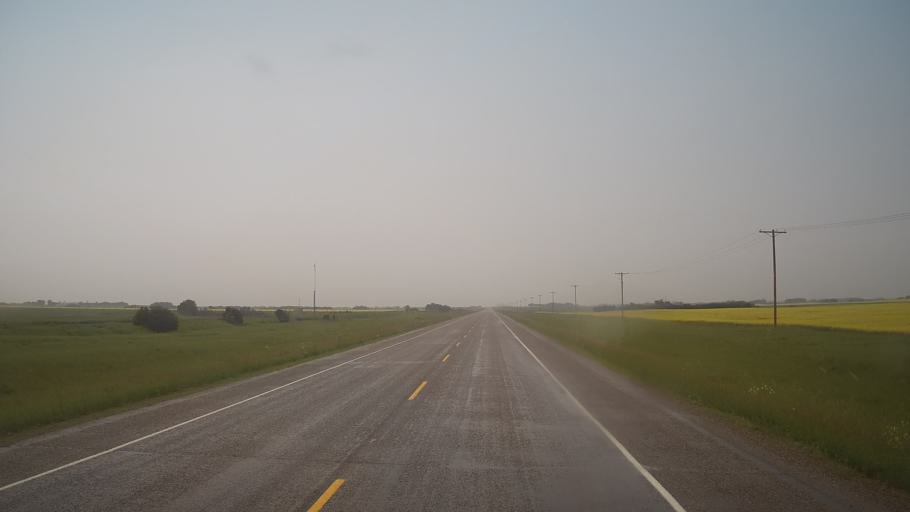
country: CA
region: Saskatchewan
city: Biggar
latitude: 52.1511
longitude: -108.2338
